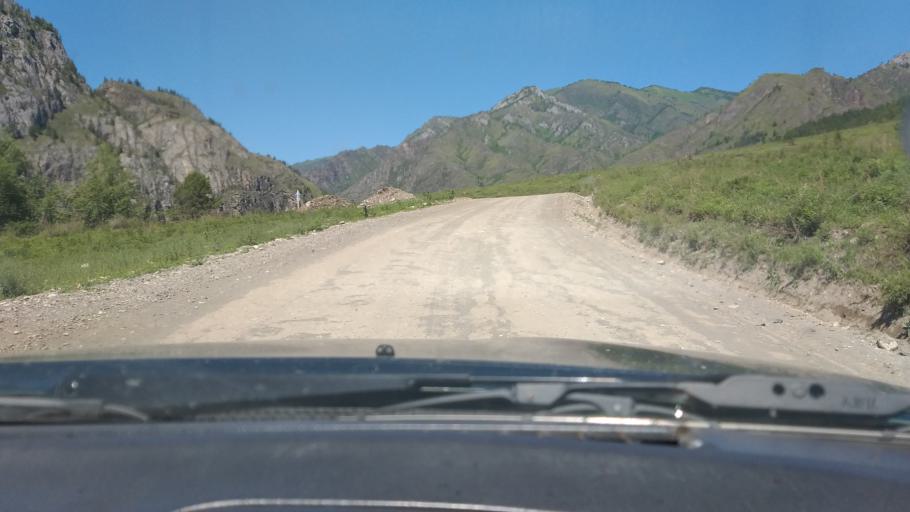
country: RU
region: Altay
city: Chemal
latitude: 51.2089
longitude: 86.0866
